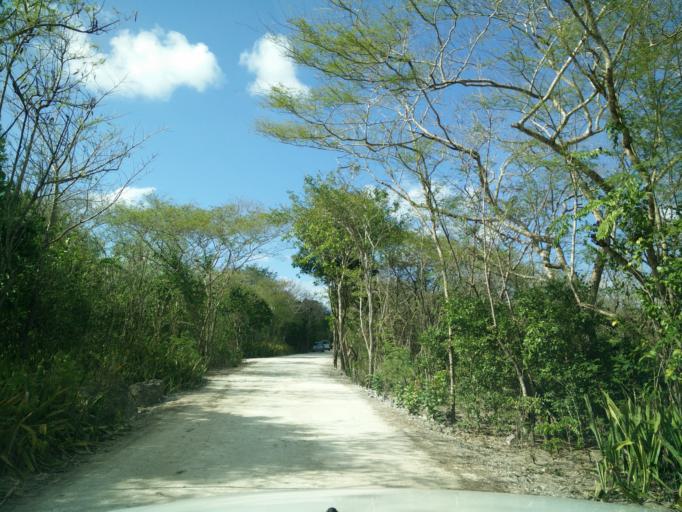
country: GP
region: Guadeloupe
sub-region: Guadeloupe
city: Port-Louis
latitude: 16.4353
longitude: -61.5366
